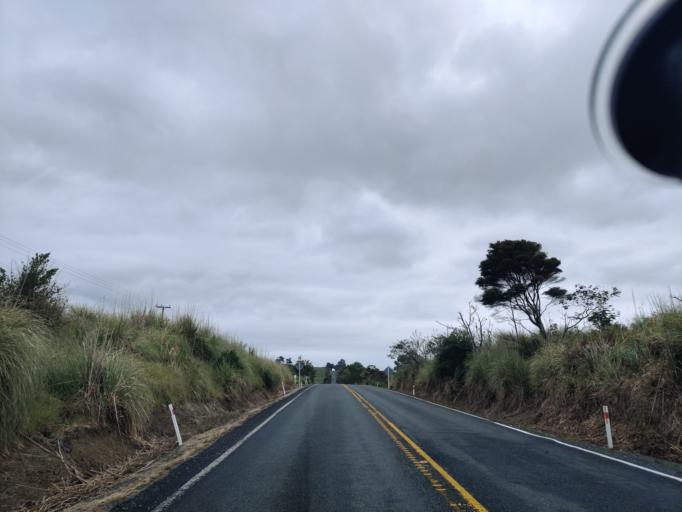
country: NZ
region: Northland
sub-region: Kaipara District
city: Dargaville
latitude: -36.1279
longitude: 174.1205
